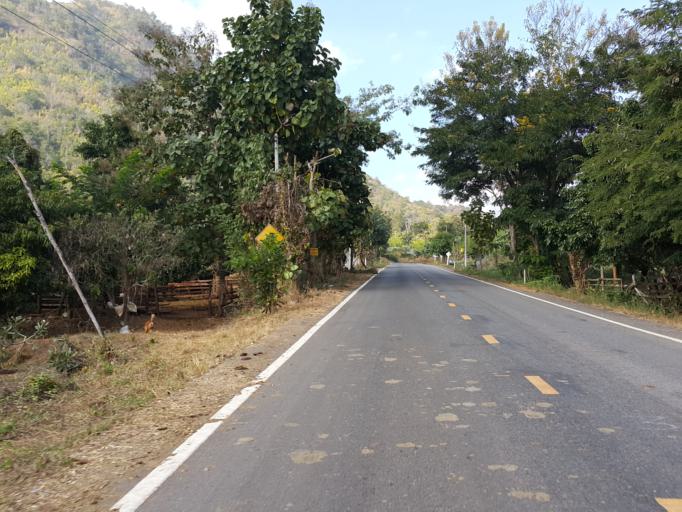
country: TH
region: Lamphun
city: Ban Hong
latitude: 18.2575
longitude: 98.9133
